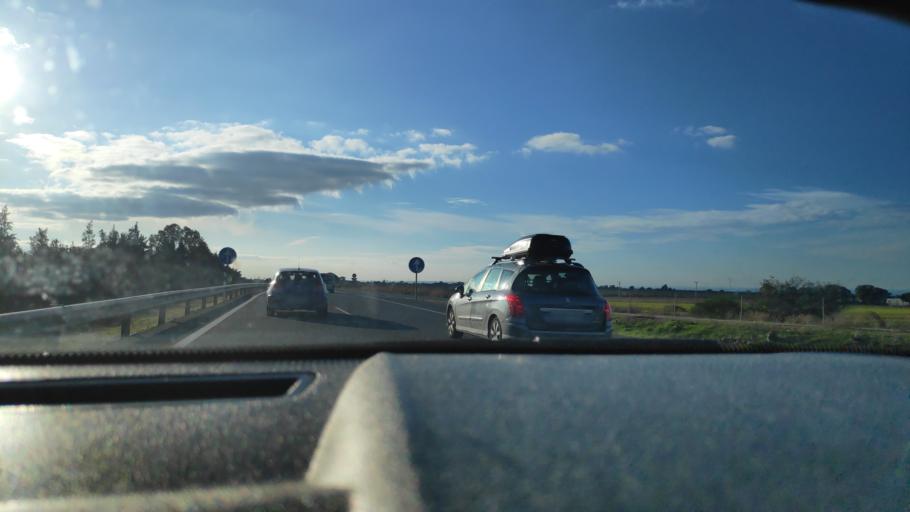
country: ES
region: Andalusia
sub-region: Provincia de Sevilla
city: El Viso del Alcor
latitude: 37.4608
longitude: -5.7372
